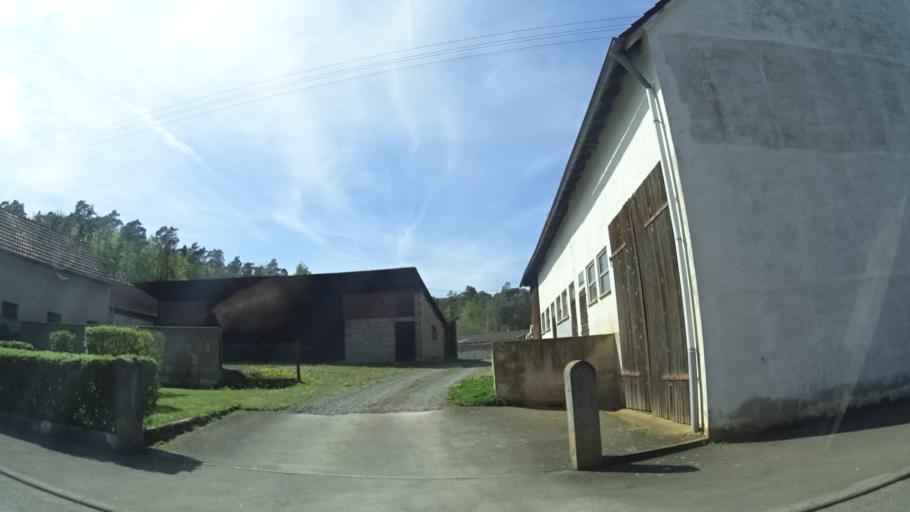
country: DE
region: Bavaria
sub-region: Regierungsbezirk Unterfranken
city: Burgpreppach
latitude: 50.1680
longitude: 10.6348
